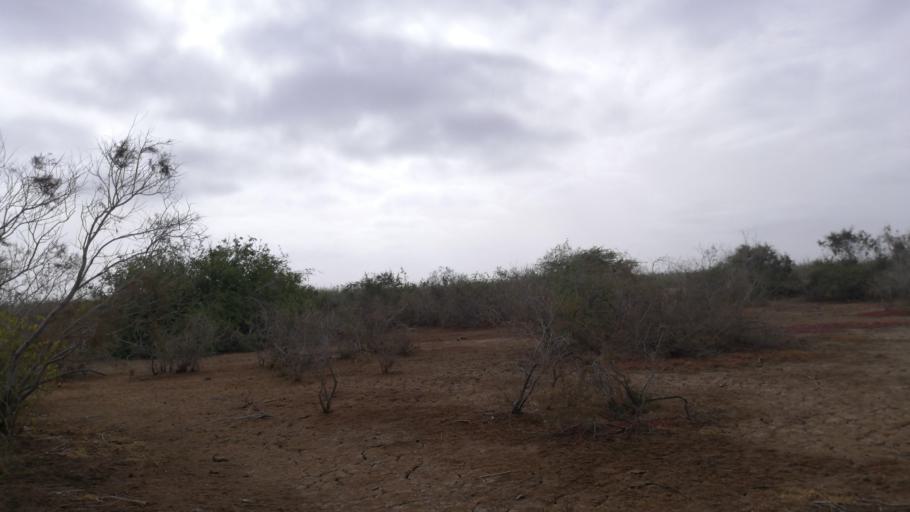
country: SN
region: Saint-Louis
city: Saint-Louis
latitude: 16.3693
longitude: -16.2572
